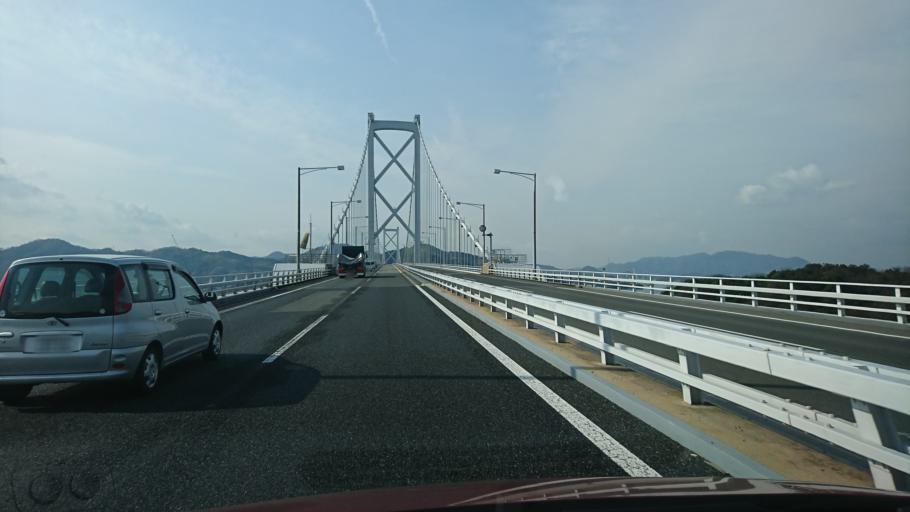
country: JP
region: Hiroshima
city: Onomichi
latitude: 34.3601
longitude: 133.1872
